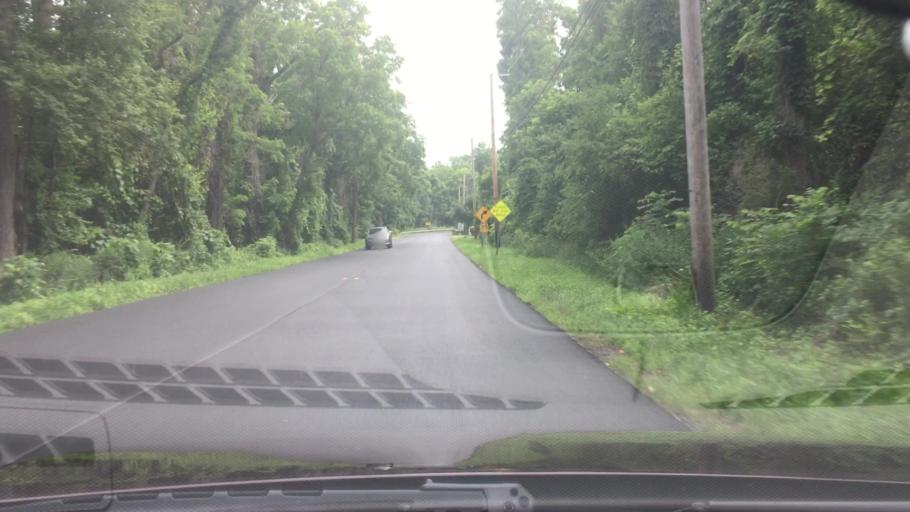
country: US
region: New York
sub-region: Dutchess County
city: Hillside Lake
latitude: 41.5706
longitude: -73.7530
